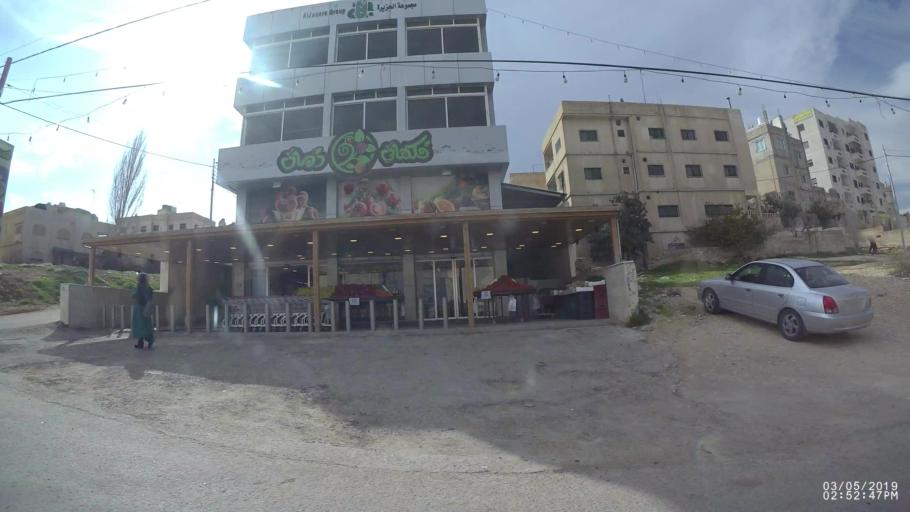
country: JO
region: Amman
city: Amman
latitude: 32.0095
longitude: 35.9522
